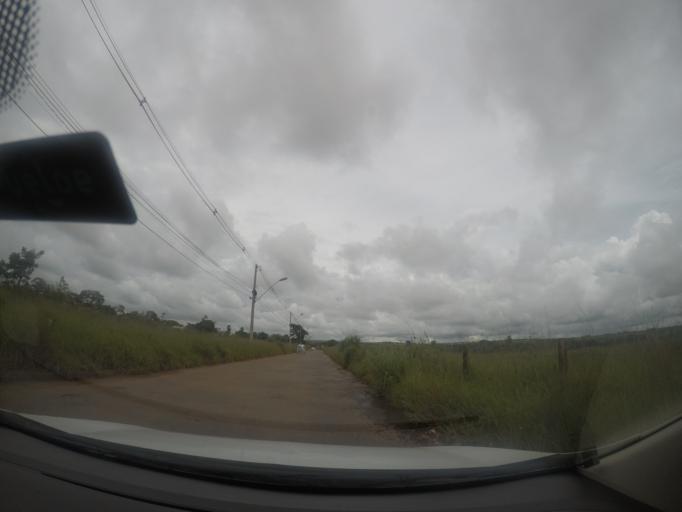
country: BR
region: Goias
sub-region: Trindade
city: Trindade
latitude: -16.6837
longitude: -49.4008
